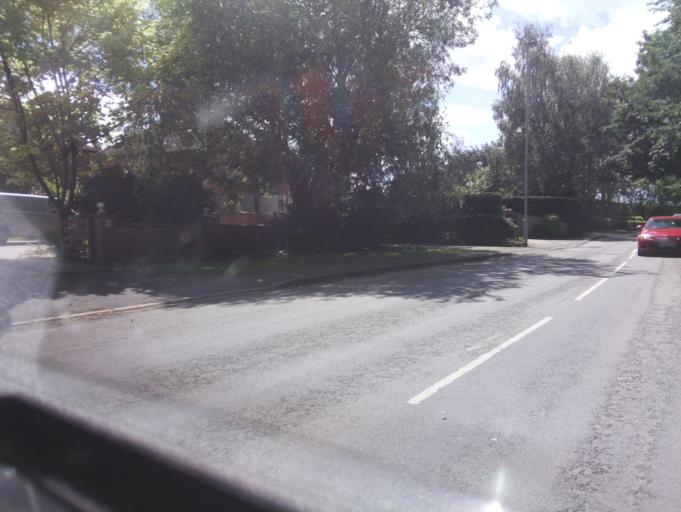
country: GB
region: England
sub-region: Nottinghamshire
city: Lowdham
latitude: 53.0123
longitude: -1.0168
